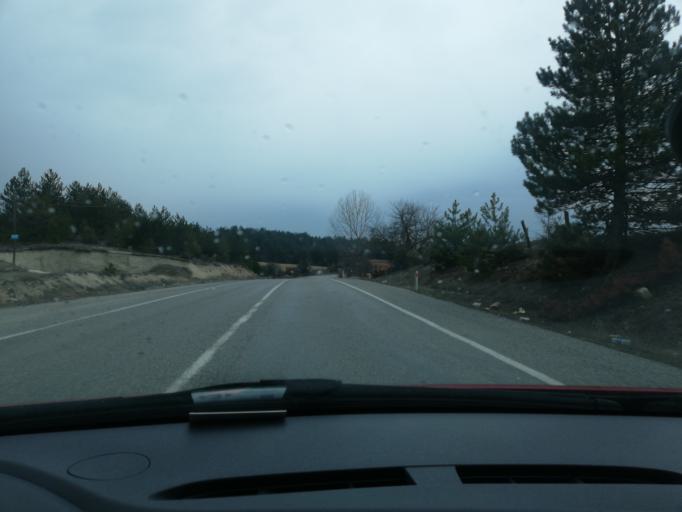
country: TR
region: Kastamonu
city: Daday
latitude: 41.4793
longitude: 33.5431
